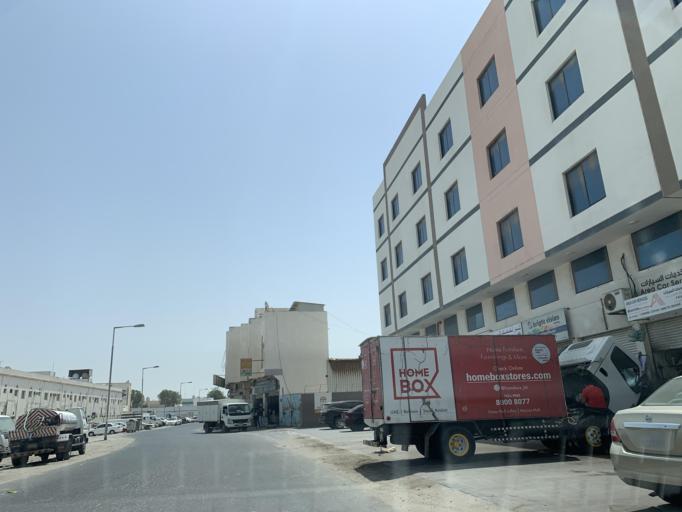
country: BH
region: Northern
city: Madinat `Isa
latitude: 26.1912
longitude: 50.5550
